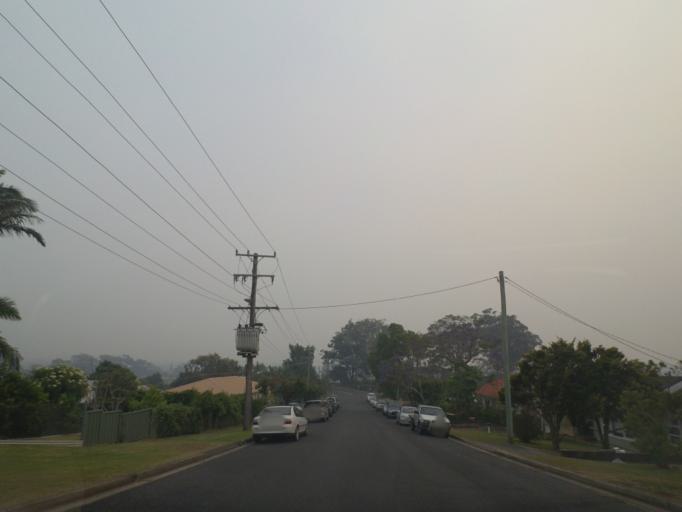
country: AU
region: New South Wales
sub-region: Coffs Harbour
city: Coffs Harbour
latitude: -30.3031
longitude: 153.1127
